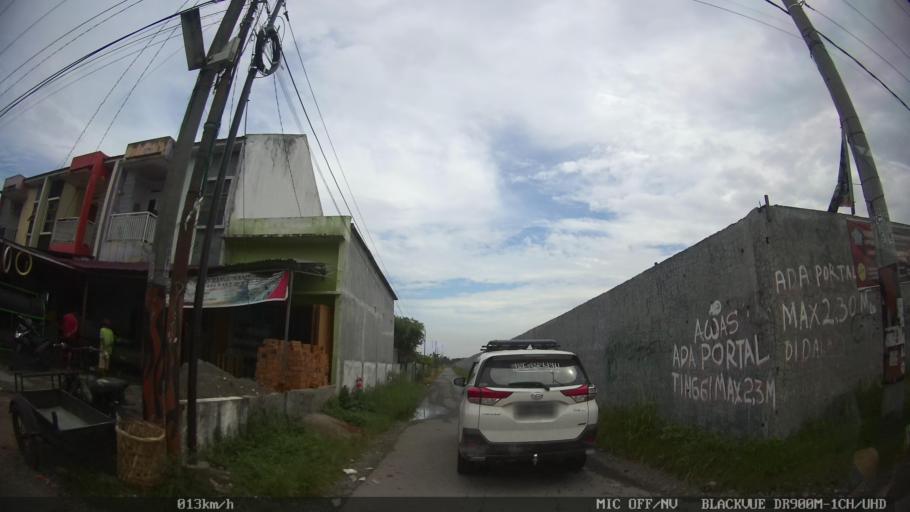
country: ID
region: North Sumatra
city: Sunggal
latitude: 3.6144
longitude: 98.5909
